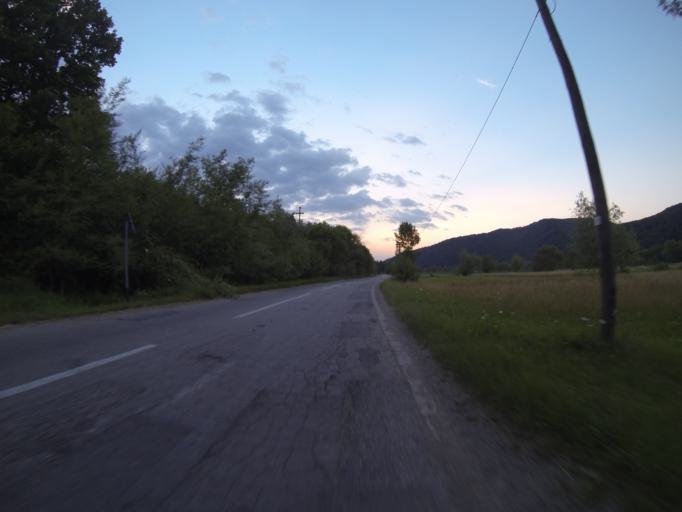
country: RO
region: Brasov
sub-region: Comuna Sinca Noua
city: Sinca Noua
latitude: 45.7304
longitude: 25.2345
